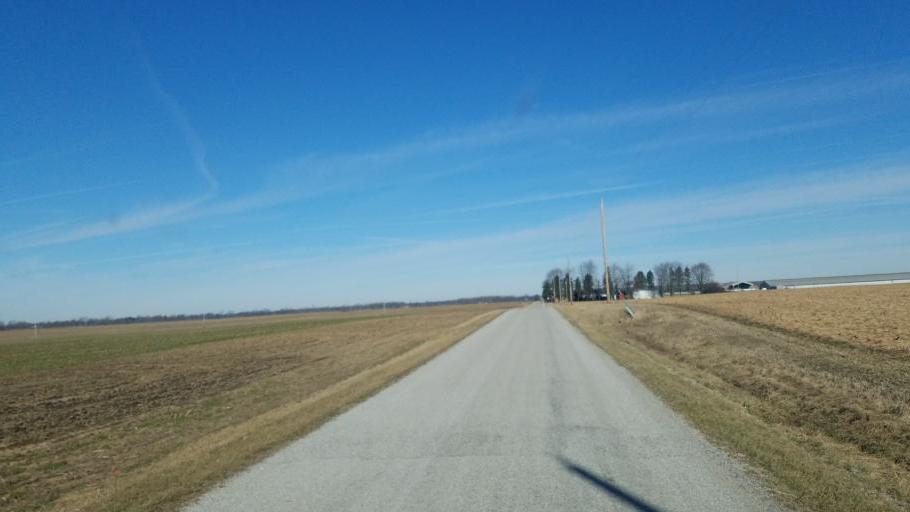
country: US
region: Ohio
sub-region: Union County
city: Richwood
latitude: 40.5237
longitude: -83.3251
